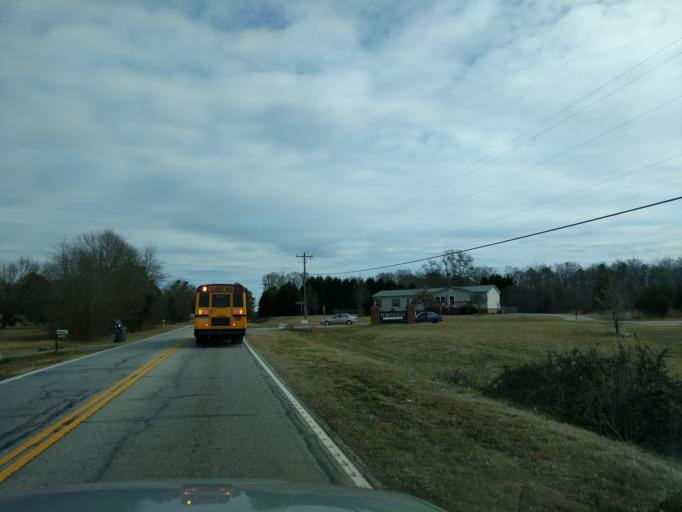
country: US
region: Georgia
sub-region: Hart County
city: Reed Creek
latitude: 34.5632
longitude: -82.8823
